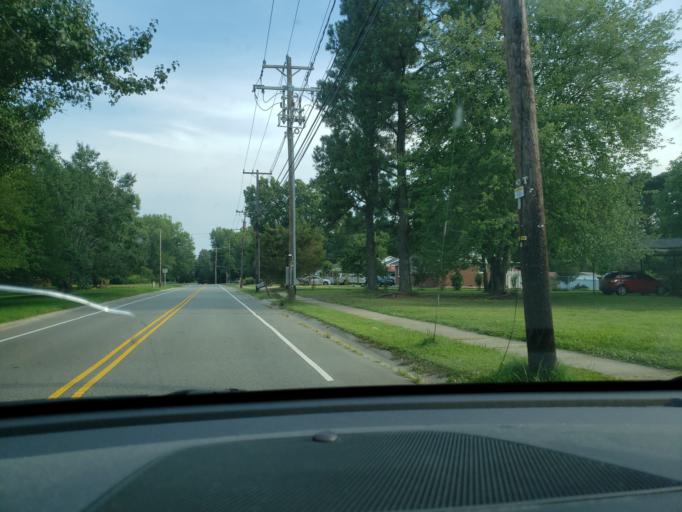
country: US
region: North Carolina
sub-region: Durham County
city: Durham
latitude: 35.9021
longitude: -78.9114
